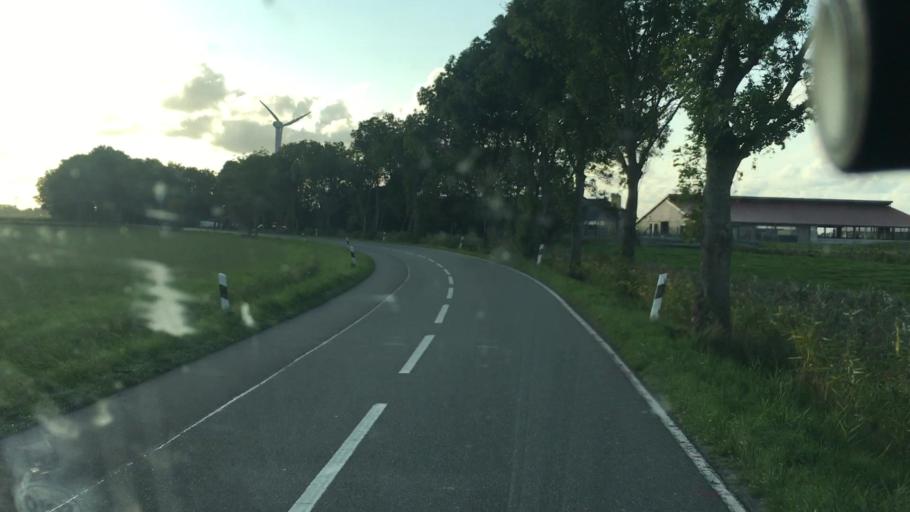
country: DE
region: Lower Saxony
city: Wittmund
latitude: 53.6429
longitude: 7.8128
